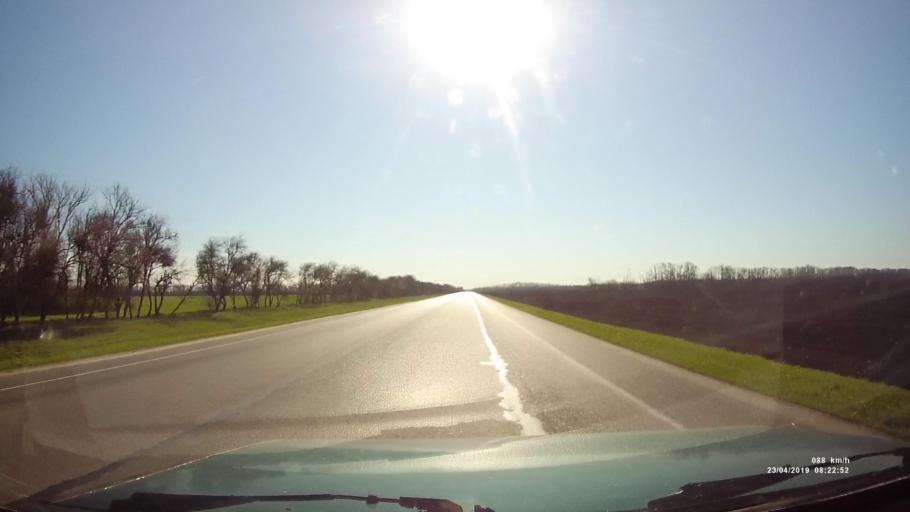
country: RU
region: Rostov
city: Tselina
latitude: 46.5342
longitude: 40.9180
